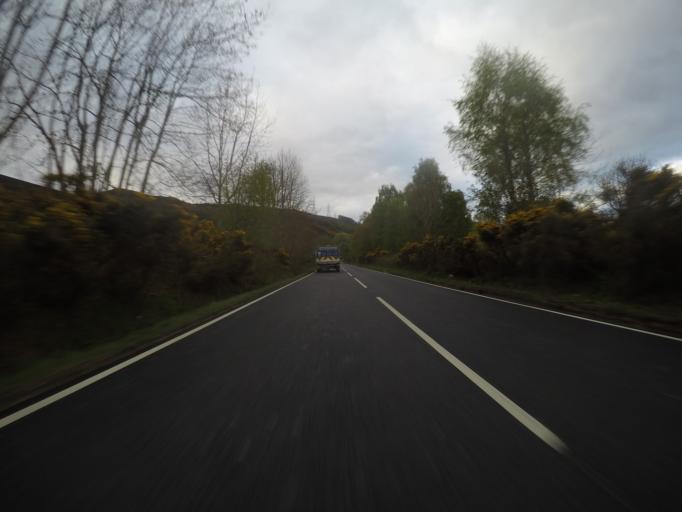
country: GB
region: Scotland
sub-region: Highland
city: Spean Bridge
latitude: 57.1274
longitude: -4.6921
